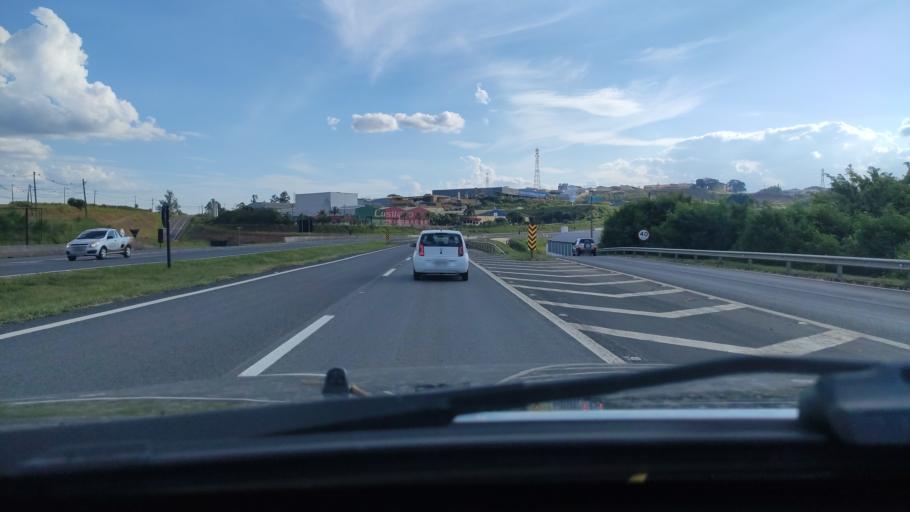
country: BR
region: Sao Paulo
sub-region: Itapira
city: Itapira
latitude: -22.4506
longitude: -46.8393
